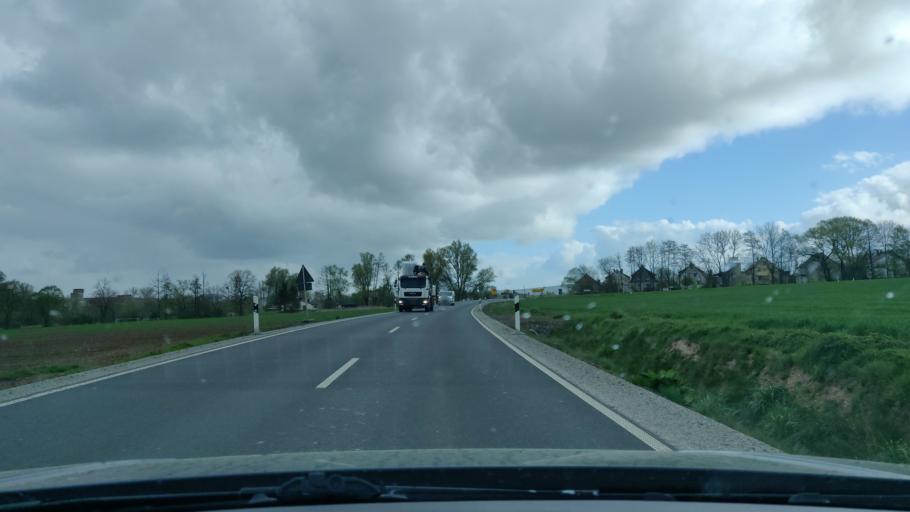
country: DE
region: Hesse
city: Felsberg
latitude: 51.1131
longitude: 9.4068
